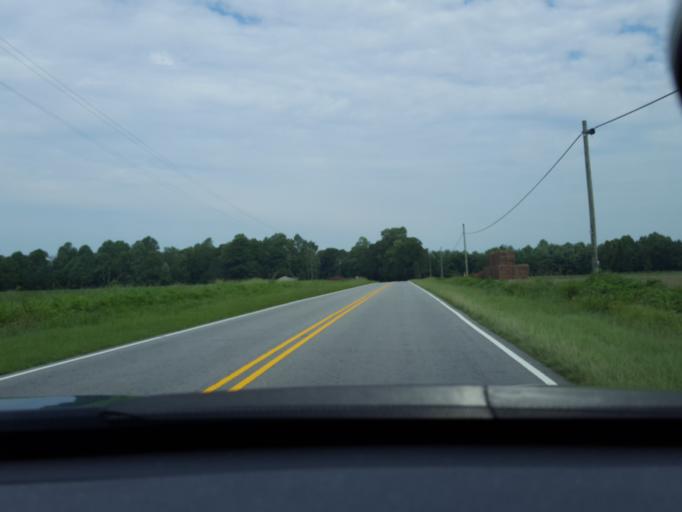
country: US
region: North Carolina
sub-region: Chowan County
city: Edenton
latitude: 36.1690
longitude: -76.6592
